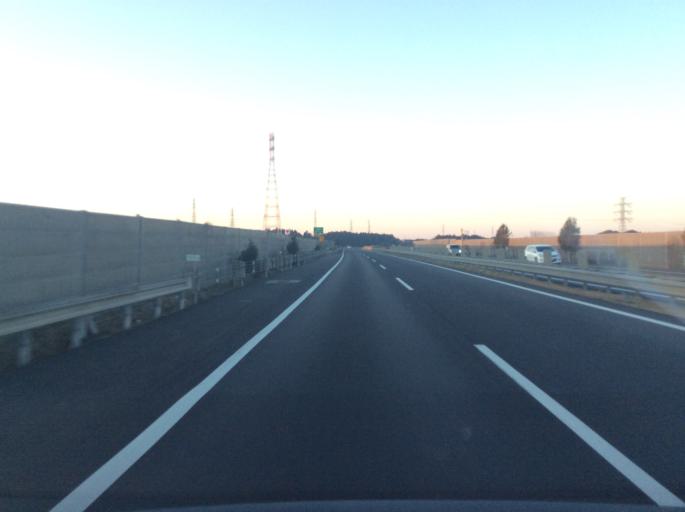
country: JP
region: Ibaraki
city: Funaishikawa
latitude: 36.4973
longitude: 140.5652
